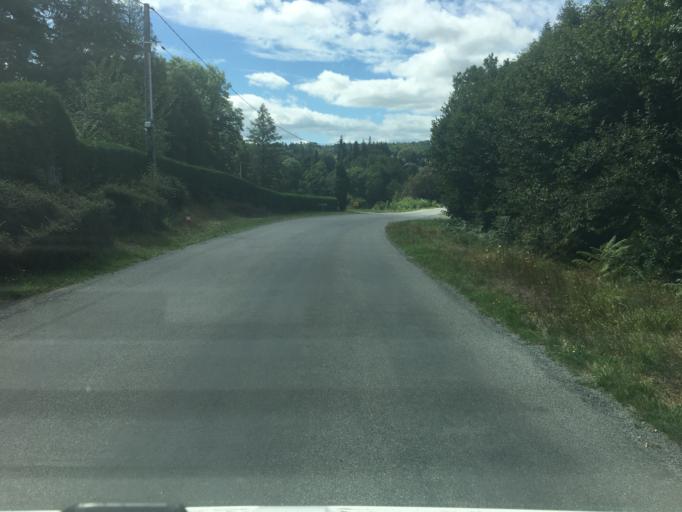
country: FR
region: Limousin
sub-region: Departement de la Correze
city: Neuvic
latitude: 45.4197
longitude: 2.3376
